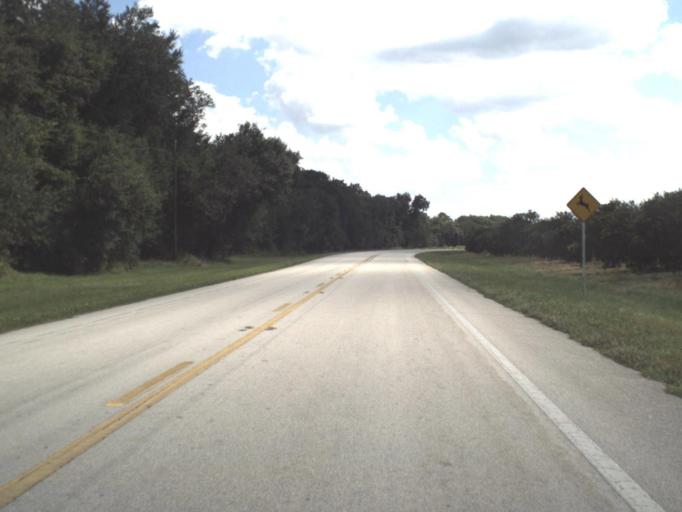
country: US
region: Florida
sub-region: Highlands County
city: Sebring
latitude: 27.4266
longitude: -81.5825
